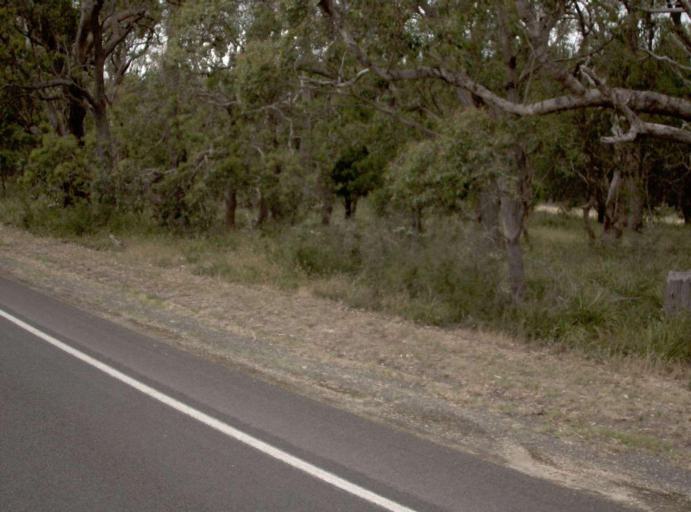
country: AU
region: Victoria
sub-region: Wellington
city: Sale
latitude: -38.2375
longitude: 147.0546
